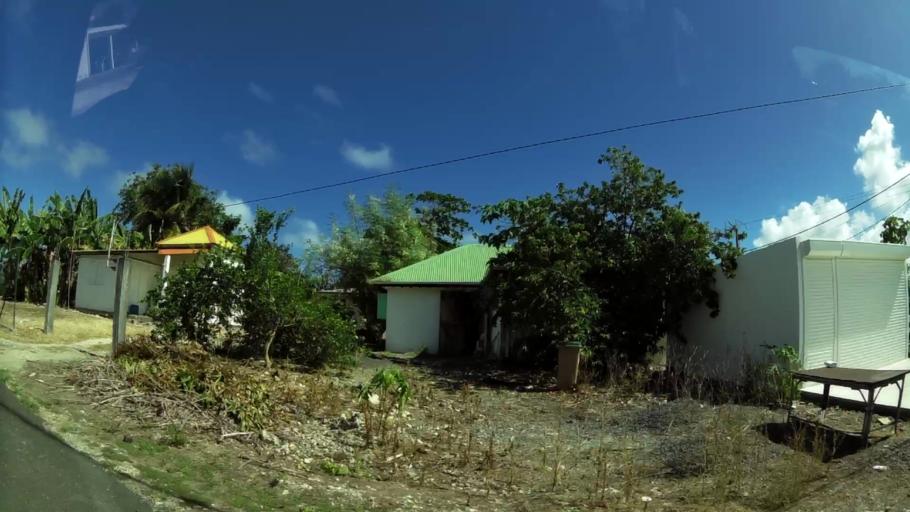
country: GP
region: Guadeloupe
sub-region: Guadeloupe
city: Petit-Canal
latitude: 16.3694
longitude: -61.4362
